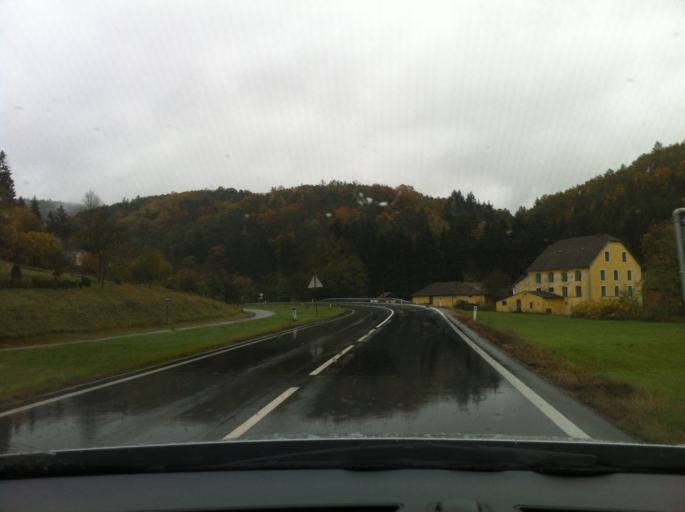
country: AT
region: Lower Austria
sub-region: Politischer Bezirk Melk
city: Leiben
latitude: 48.2449
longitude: 15.2858
